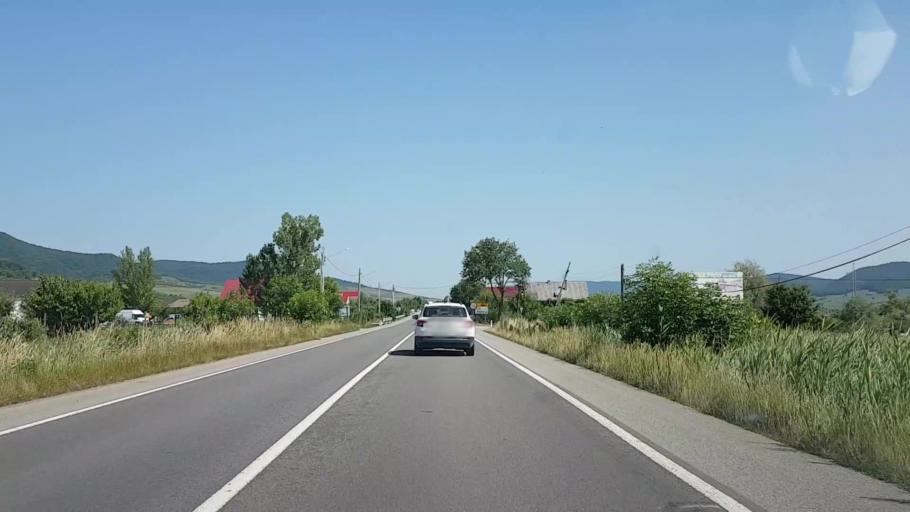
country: RO
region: Bistrita-Nasaud
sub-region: Comuna Sieu-Magherus
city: Sieu-Magherus
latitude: 47.1010
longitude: 24.3600
